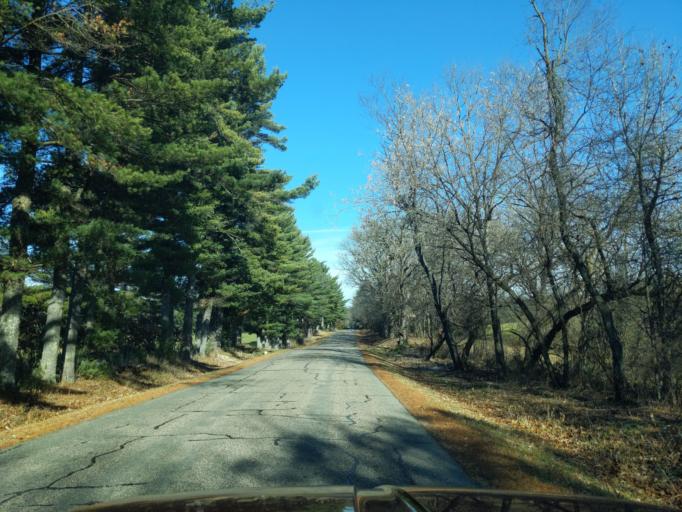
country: US
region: Wisconsin
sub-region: Waushara County
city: Silver Lake
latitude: 44.0775
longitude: -89.1940
